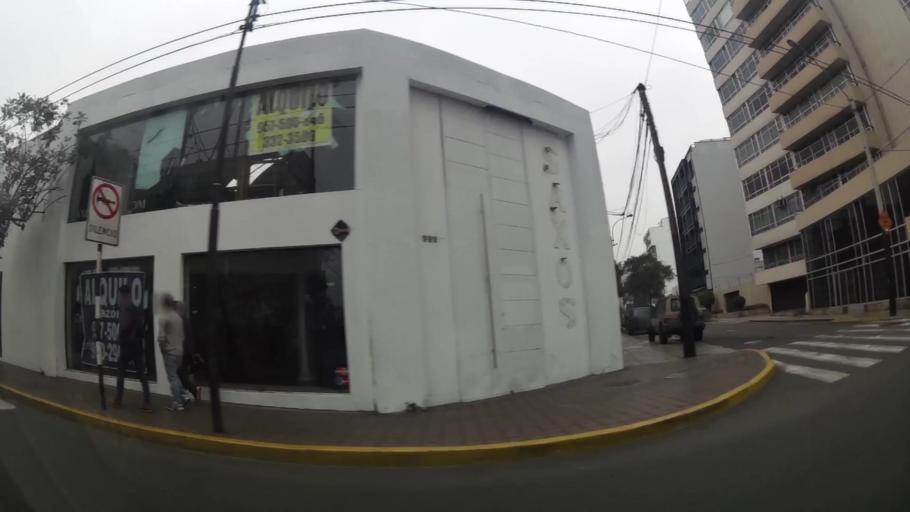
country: PE
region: Lima
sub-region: Lima
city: San Isidro
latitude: -12.1277
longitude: -77.0295
